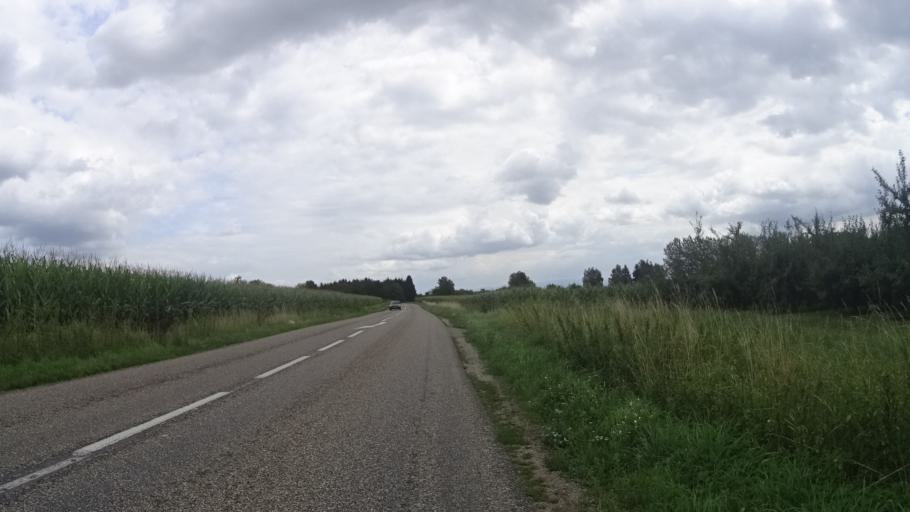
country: FR
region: Alsace
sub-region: Departement du Bas-Rhin
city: Geudertheim
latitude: 48.7245
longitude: 7.7323
